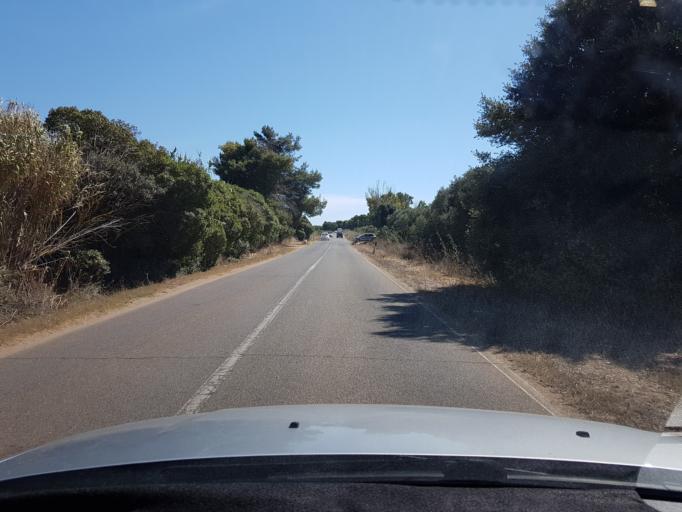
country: IT
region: Sardinia
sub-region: Provincia di Oristano
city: Cabras
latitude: 39.9025
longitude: 8.4362
